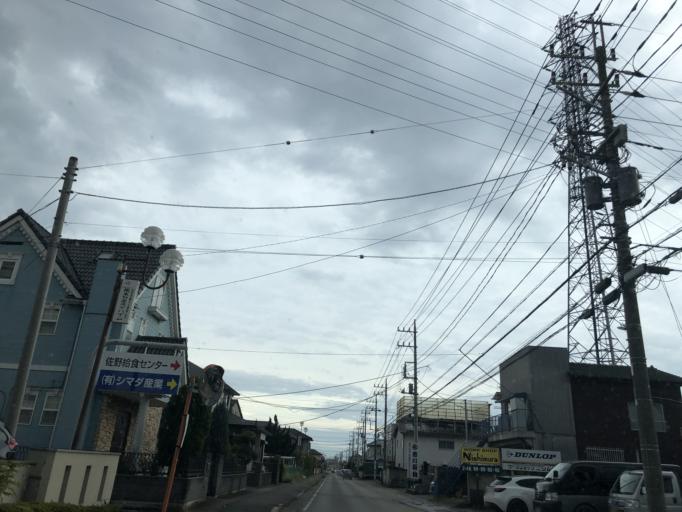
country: JP
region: Tochigi
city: Sano
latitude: 36.3213
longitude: 139.5711
